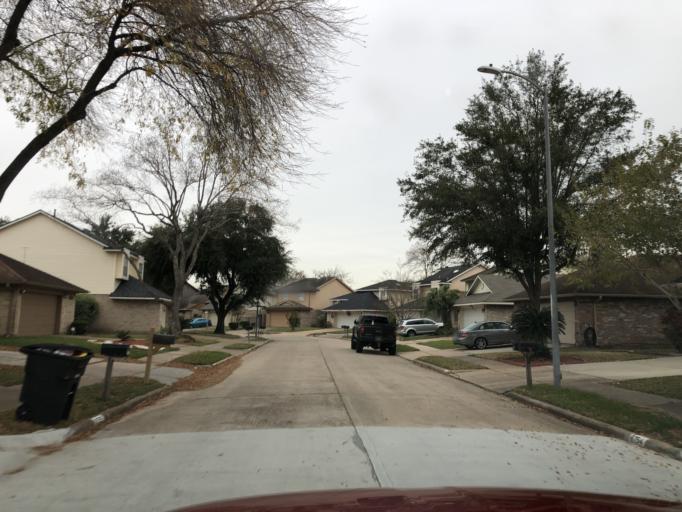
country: US
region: Texas
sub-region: Fort Bend County
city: Missouri City
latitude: 29.6421
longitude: -95.5317
